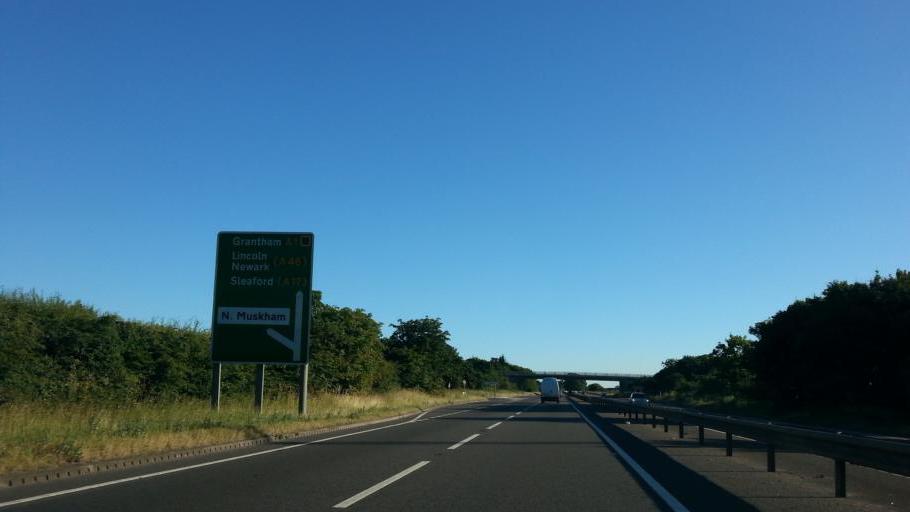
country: GB
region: England
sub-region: Nottinghamshire
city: South Collingham
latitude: 53.1288
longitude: -0.8126
